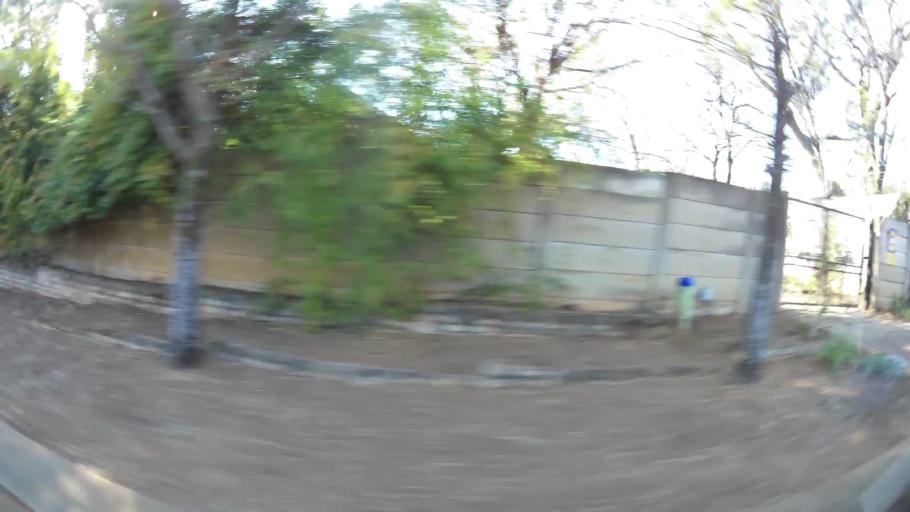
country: ZA
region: Gauteng
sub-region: City of Johannesburg Metropolitan Municipality
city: Midrand
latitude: -26.0711
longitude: 28.0387
